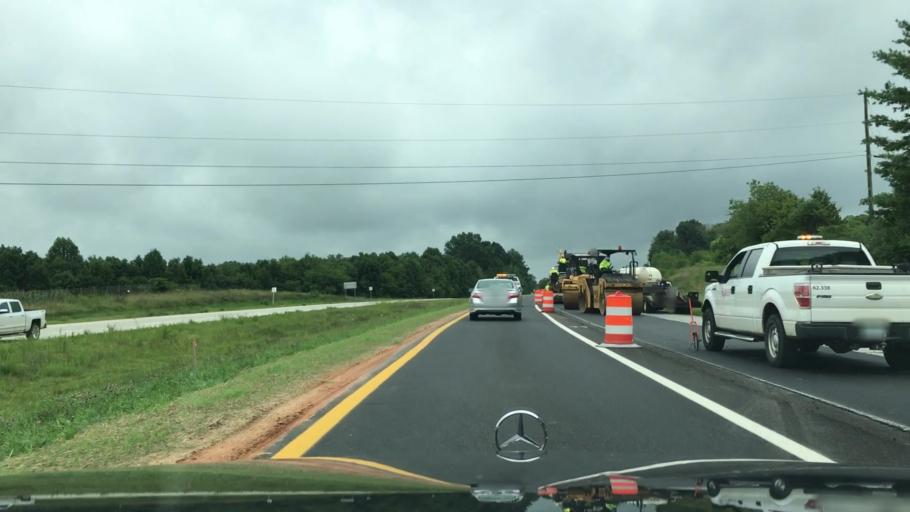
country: US
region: Virginia
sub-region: Appomattox County
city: Appomattox
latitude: 37.3625
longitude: -78.8168
